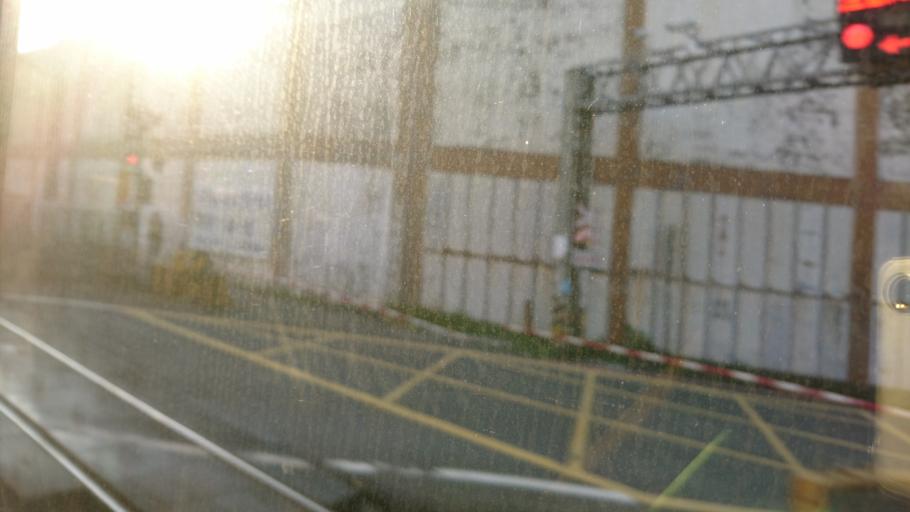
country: TW
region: Taiwan
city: Taoyuan City
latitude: 24.9497
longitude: 121.2199
